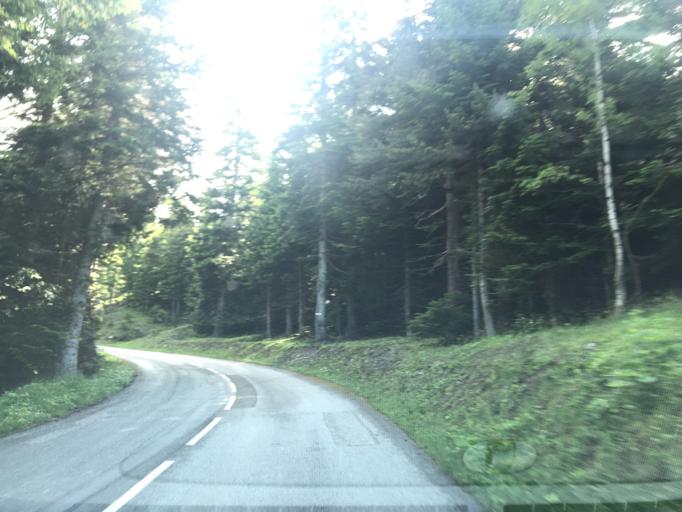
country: FR
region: Rhone-Alpes
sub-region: Departement de la Savoie
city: Modane
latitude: 45.2098
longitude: 6.6463
